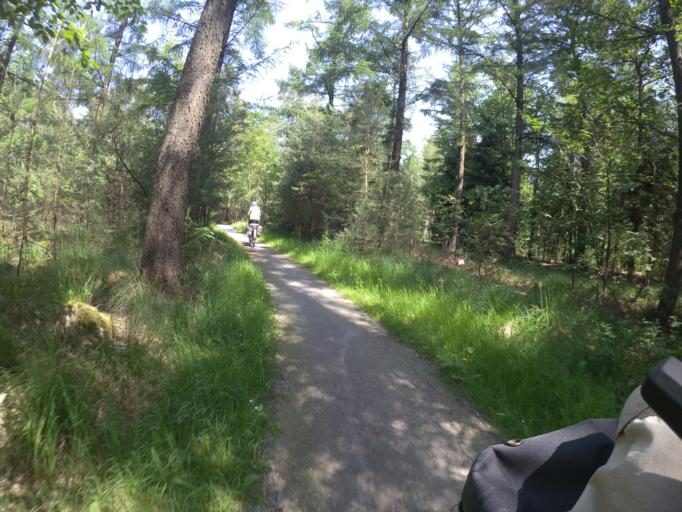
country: NL
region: Drenthe
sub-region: Gemeente De Wolden
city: Ruinen
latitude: 52.7442
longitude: 6.3979
